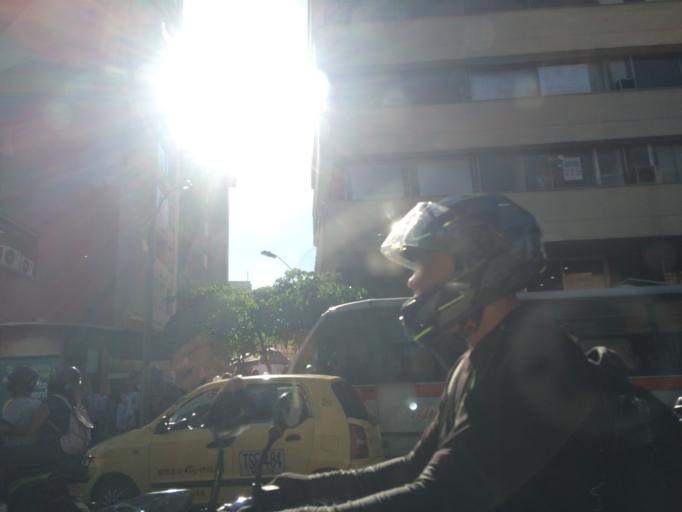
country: CO
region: Antioquia
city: Medellin
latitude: 6.2479
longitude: -75.5656
